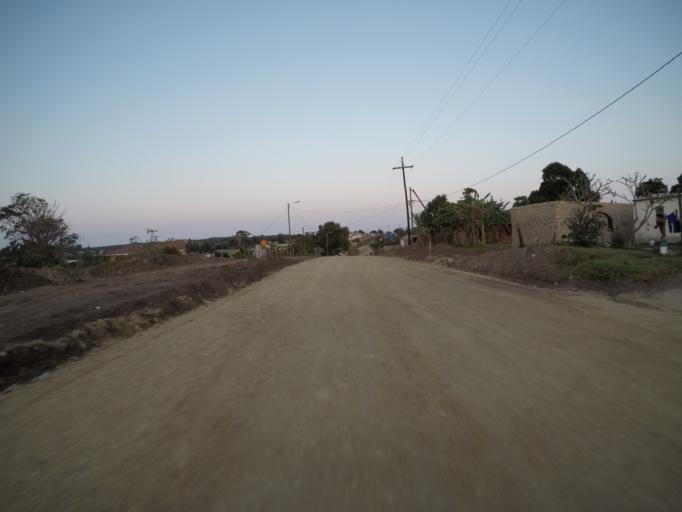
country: ZA
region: KwaZulu-Natal
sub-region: uThungulu District Municipality
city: Richards Bay
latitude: -28.7568
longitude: 32.1307
